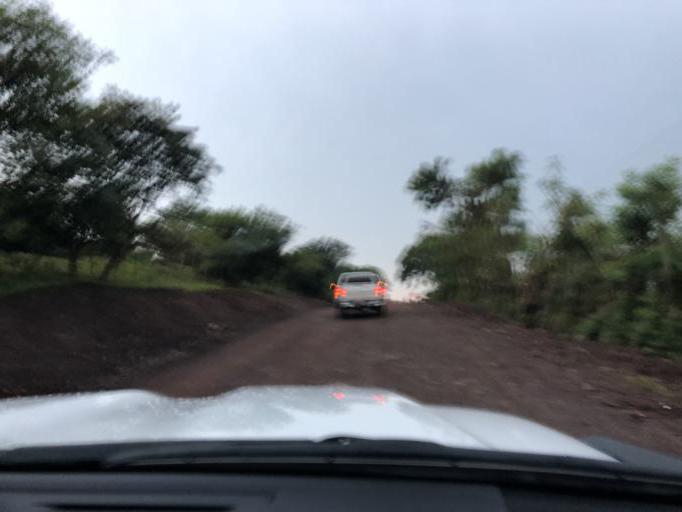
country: NI
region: Chontales
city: La Libertad
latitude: 12.1764
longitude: -85.1753
